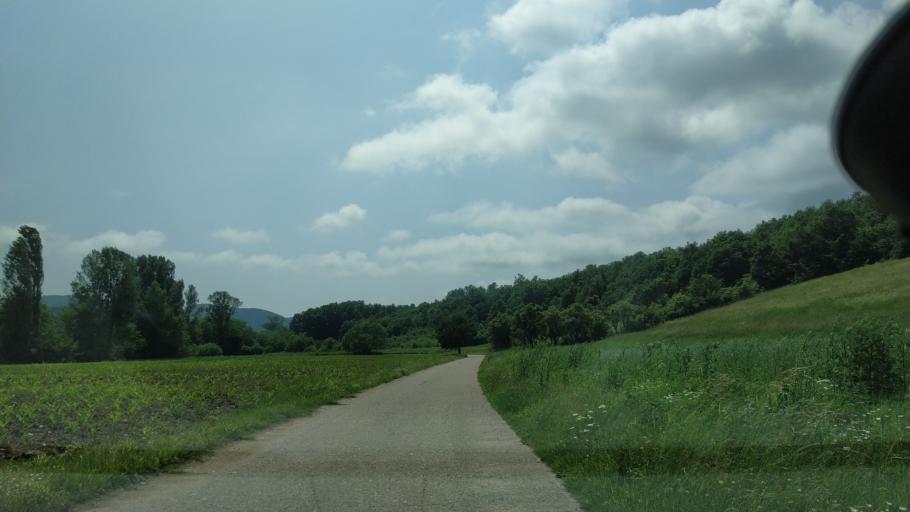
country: RS
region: Central Serbia
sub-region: Nisavski Okrug
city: Aleksinac
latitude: 43.4248
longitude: 21.7214
